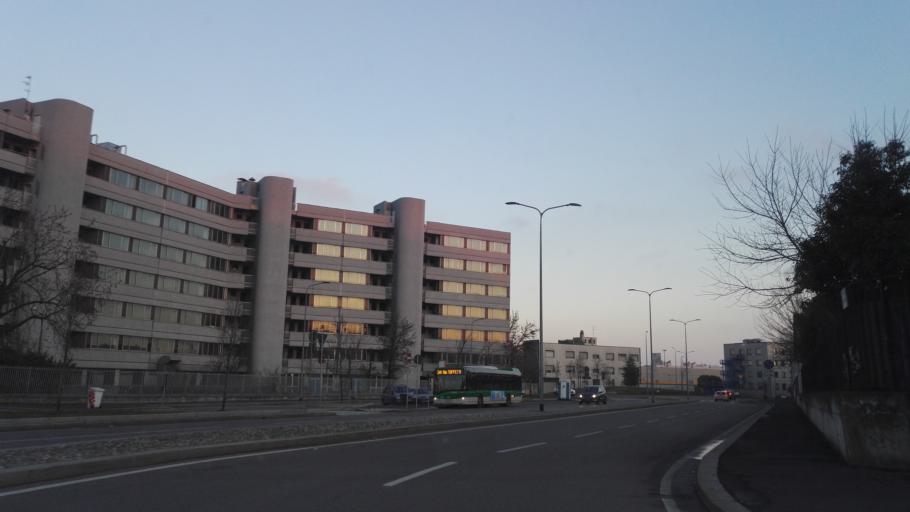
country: IT
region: Lombardy
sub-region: Citta metropolitana di Milano
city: Chiaravalle
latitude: 45.4445
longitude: 9.2301
